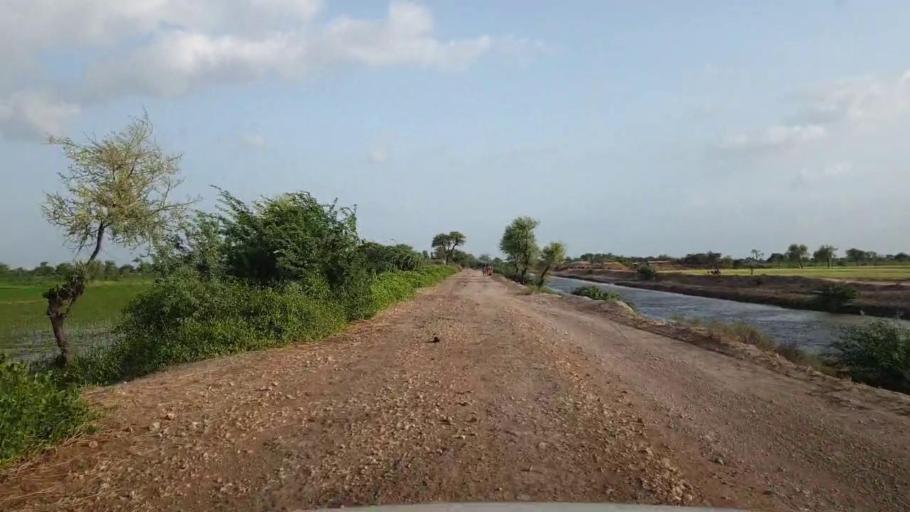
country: PK
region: Sindh
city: Kario
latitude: 24.8029
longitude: 68.6473
